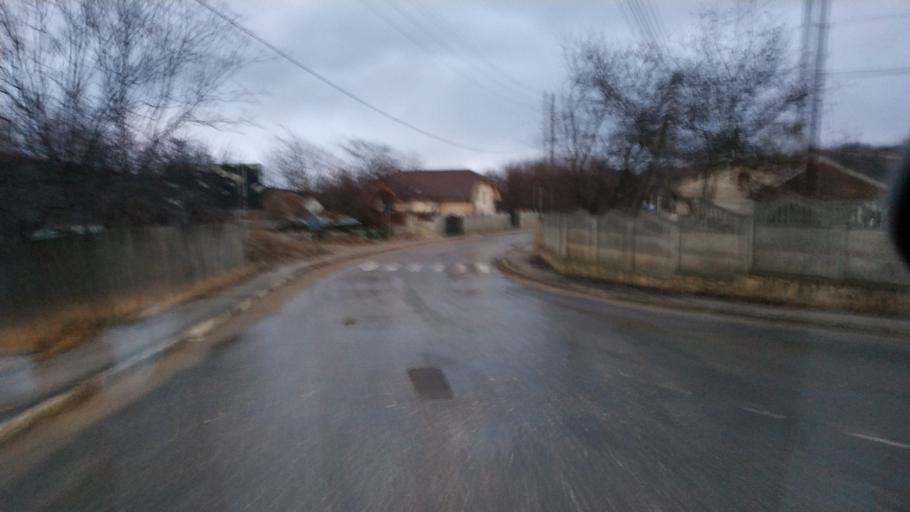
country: MD
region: Taraclia
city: Telenesti
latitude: 47.3732
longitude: 28.3673
